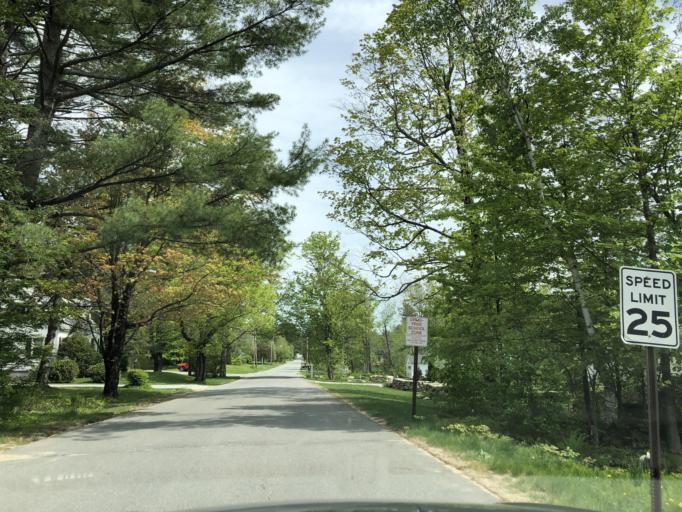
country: US
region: New Hampshire
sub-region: Merrimack County
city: New London
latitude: 43.4189
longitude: -71.9932
